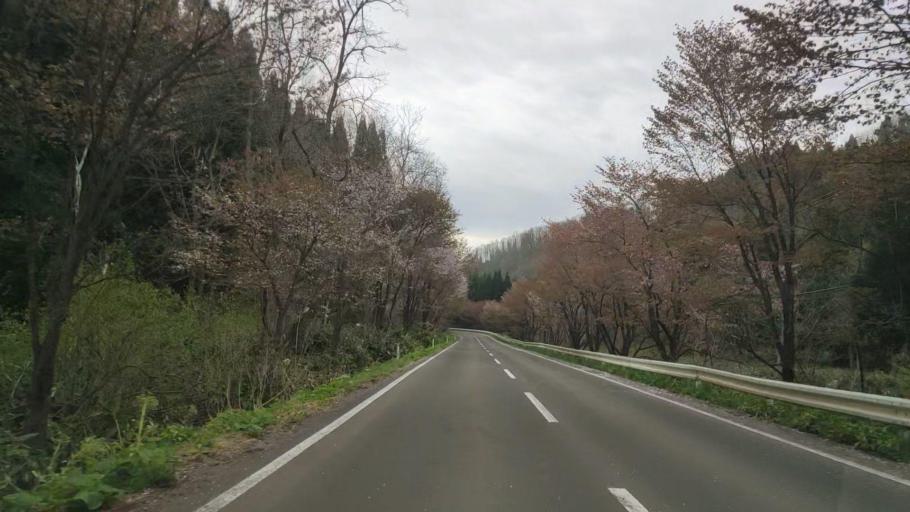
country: JP
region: Akita
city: Hanawa
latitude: 40.3510
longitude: 140.7762
